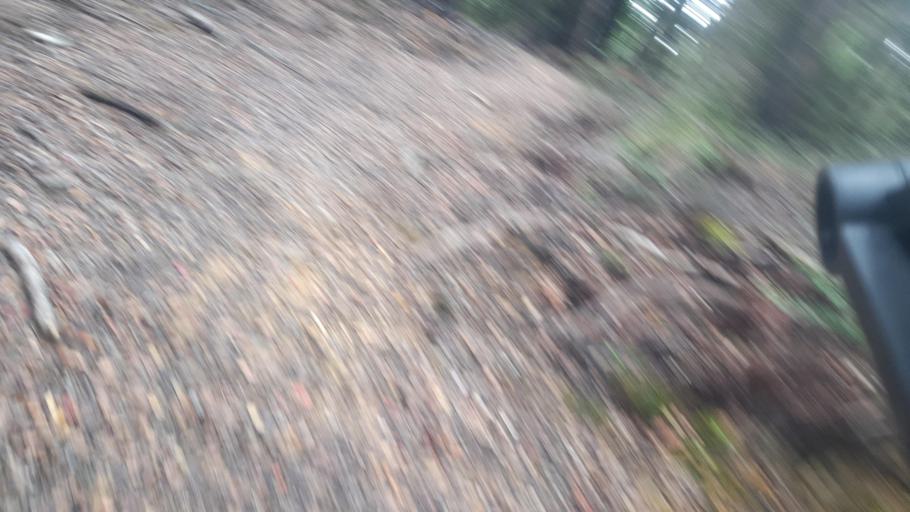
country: NZ
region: Tasman
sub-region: Tasman District
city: Wakefield
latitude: -41.7682
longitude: 172.8166
